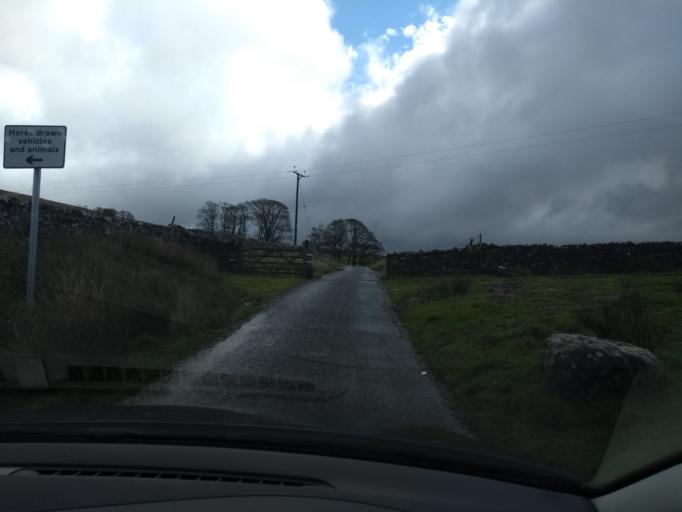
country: GB
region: England
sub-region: North Yorkshire
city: Settle
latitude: 54.1072
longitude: -2.2321
